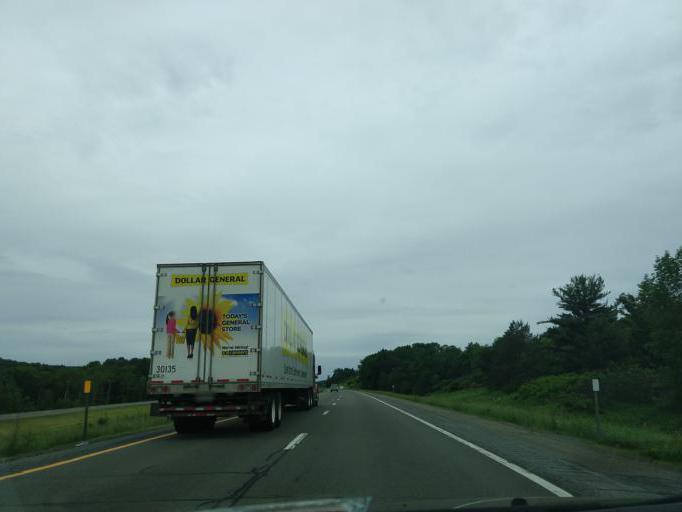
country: US
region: New York
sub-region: Broome County
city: Chenango Bridge
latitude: 42.2483
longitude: -75.9185
